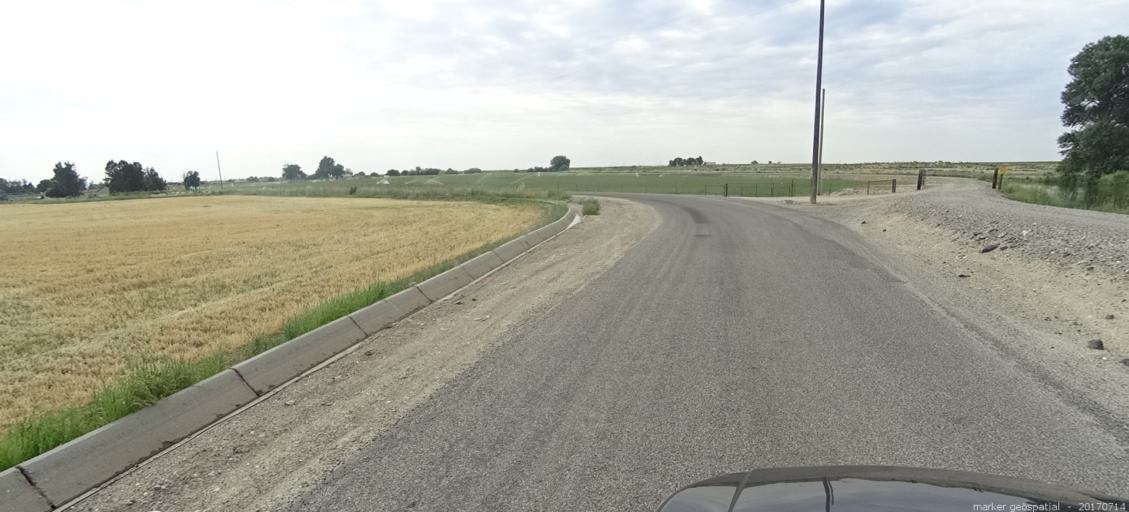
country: US
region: Idaho
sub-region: Ada County
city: Kuna
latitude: 43.4598
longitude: -116.3638
